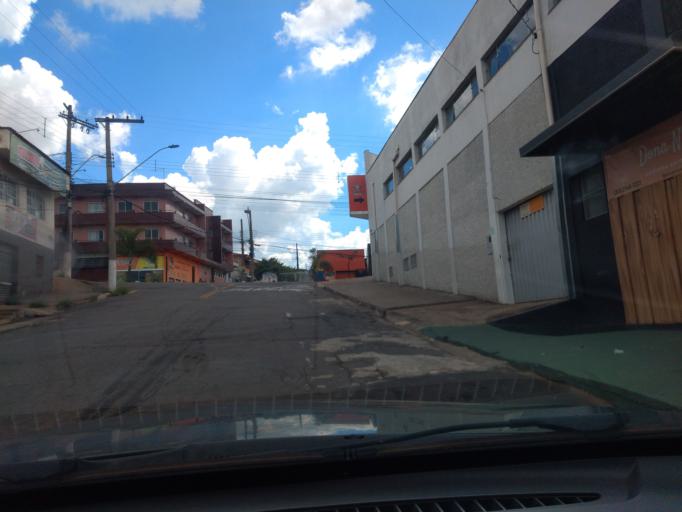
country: BR
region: Minas Gerais
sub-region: Tres Coracoes
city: Tres Coracoes
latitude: -21.6853
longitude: -45.2622
